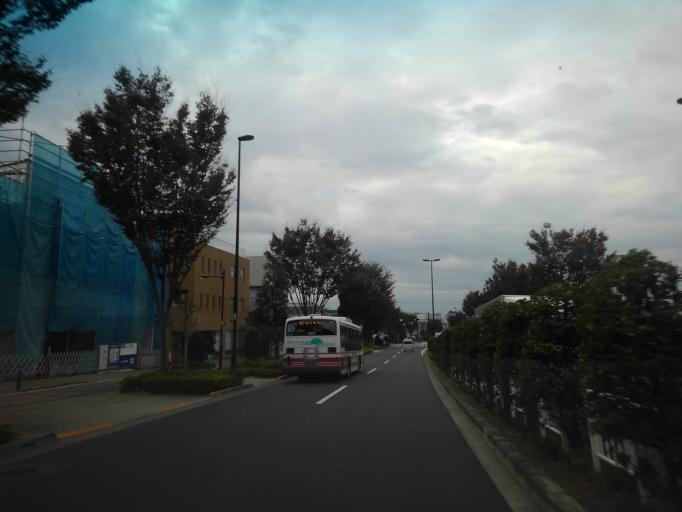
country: JP
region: Tokyo
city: Chofugaoka
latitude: 35.6692
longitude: 139.5446
